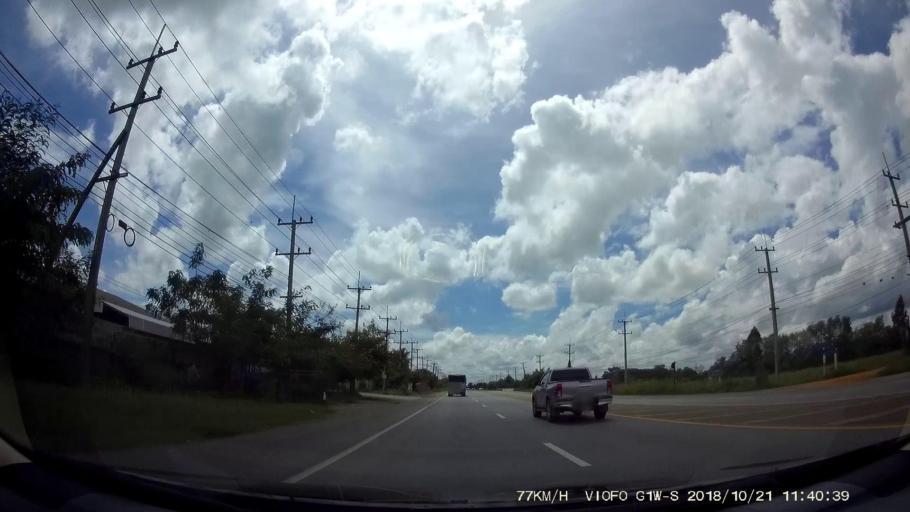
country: TH
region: Chaiyaphum
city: Chaiyaphum
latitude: 15.7105
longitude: 102.0155
